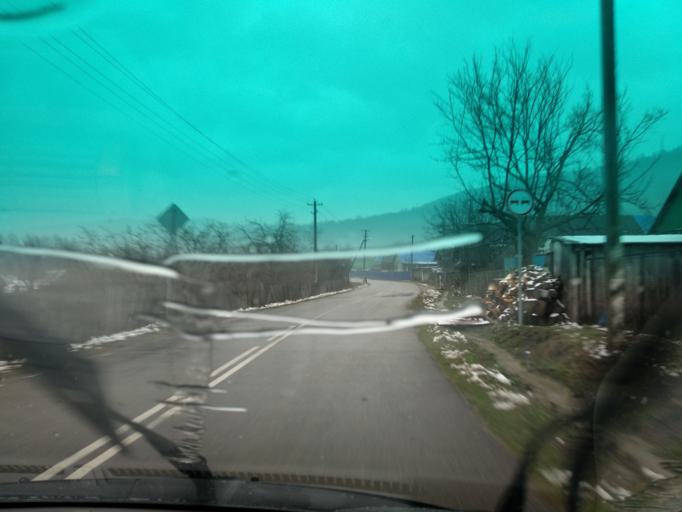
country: RU
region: Krasnodarskiy
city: Khadyzhensk
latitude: 44.2453
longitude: 39.3757
